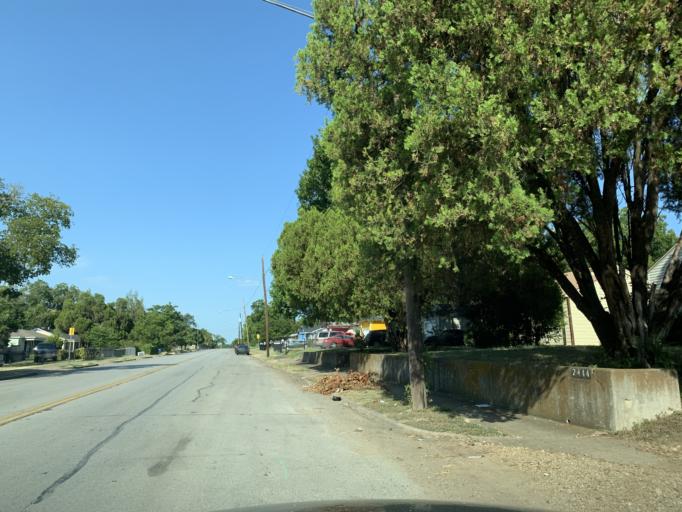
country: US
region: Texas
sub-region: Dallas County
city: Dallas
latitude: 32.7091
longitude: -96.7896
